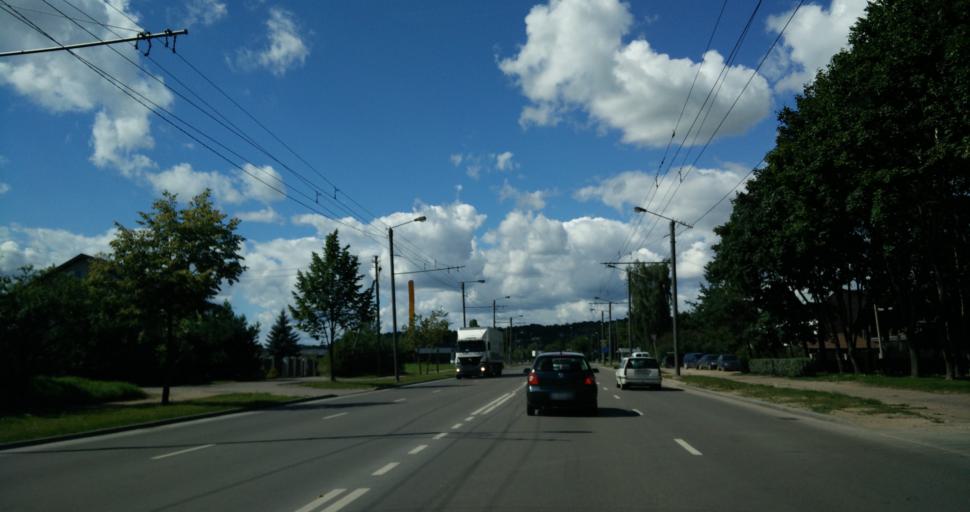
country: LT
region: Kauno apskritis
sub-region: Kauno rajonas
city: Akademija (Kaunas)
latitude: 54.9179
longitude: 23.8320
